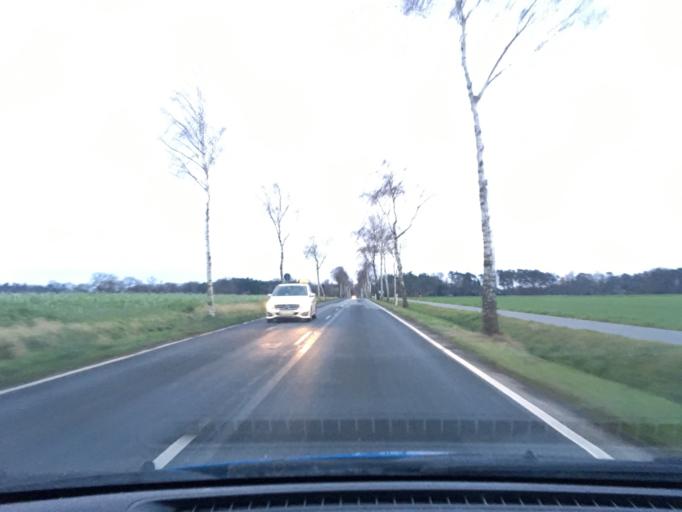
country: DE
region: Lower Saxony
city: Celle
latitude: 52.6432
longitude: 10.0602
